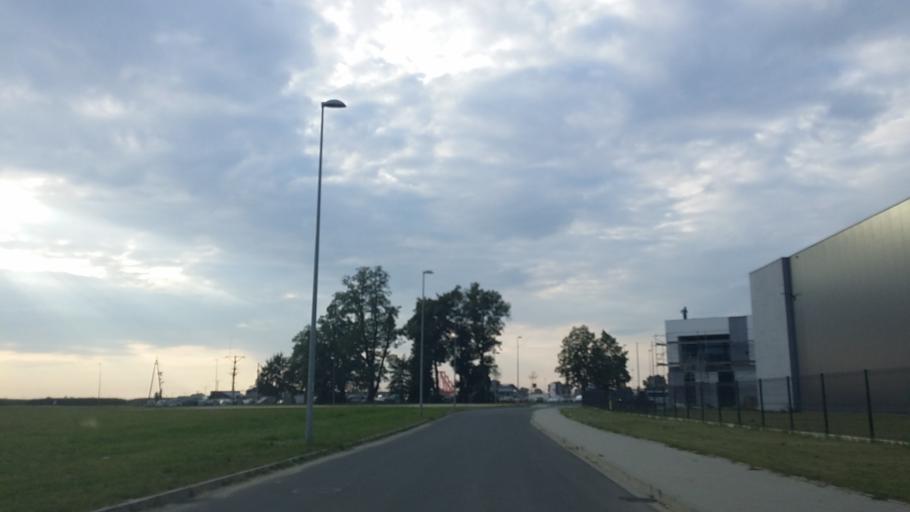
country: PL
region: Lesser Poland Voivodeship
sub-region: Powiat oswiecimski
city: Zator
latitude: 49.9968
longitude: 19.4151
